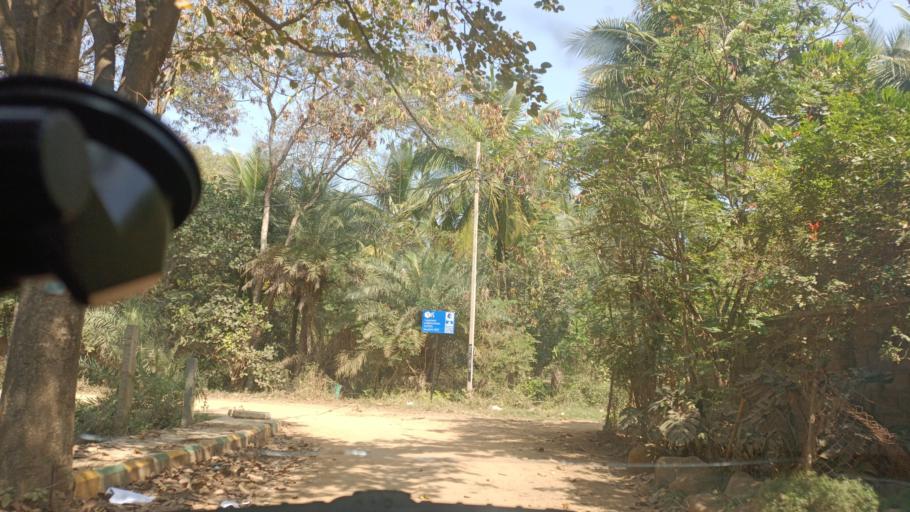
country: IN
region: Karnataka
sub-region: Bangalore Urban
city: Yelahanka
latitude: 13.1172
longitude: 77.6009
